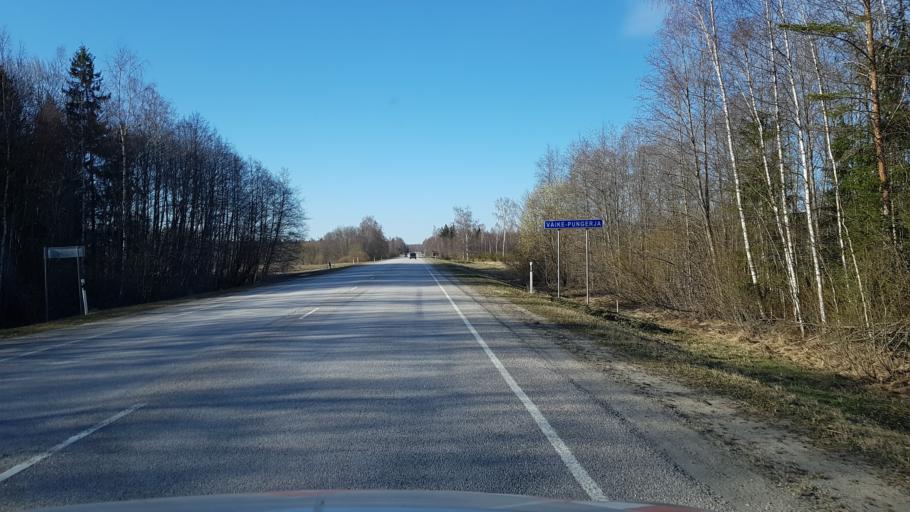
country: EE
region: Ida-Virumaa
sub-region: Johvi vald
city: Johvi
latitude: 59.1706
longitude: 27.3512
